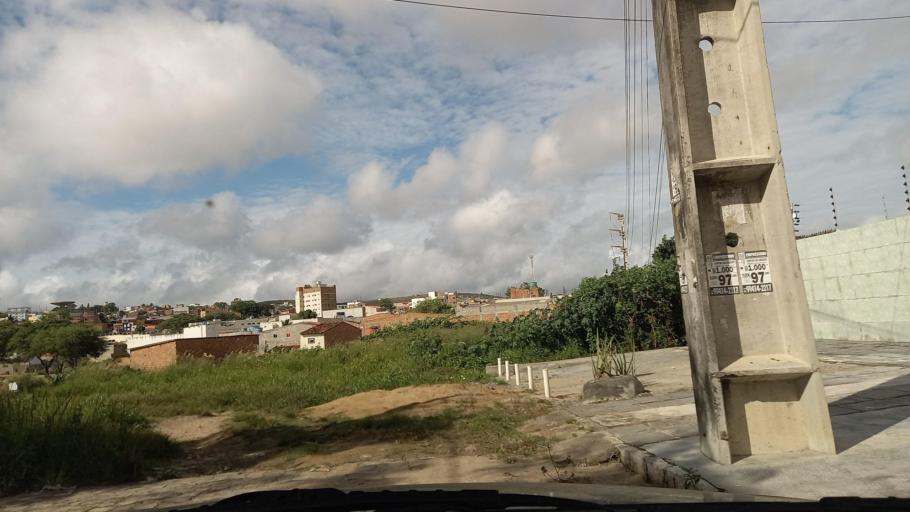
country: BR
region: Pernambuco
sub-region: Caruaru
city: Caruaru
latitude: -8.2909
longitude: -35.9831
